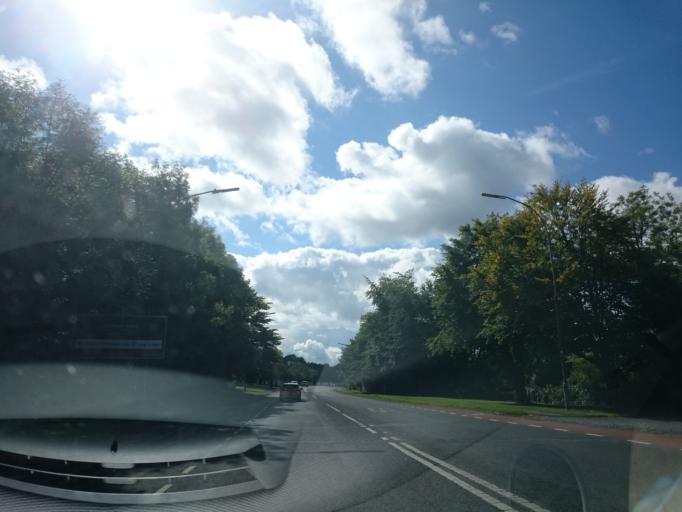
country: IE
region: Leinster
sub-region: Kilkenny
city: Kilkenny
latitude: 52.6713
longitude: -7.2533
